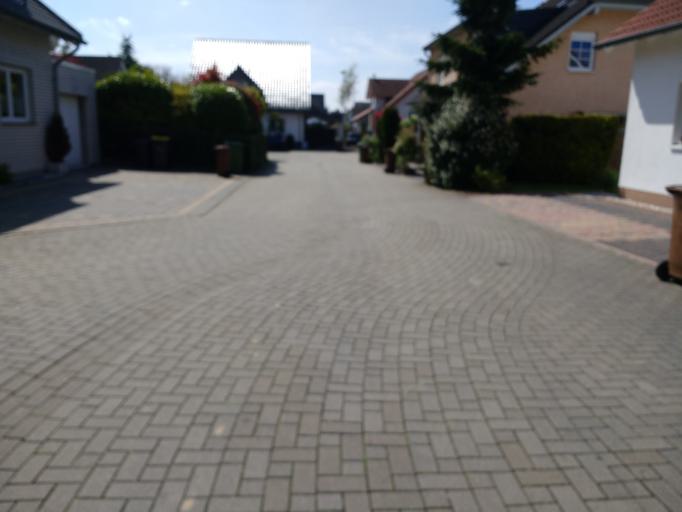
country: DE
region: North Rhine-Westphalia
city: Bornheim
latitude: 50.7184
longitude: 6.9213
